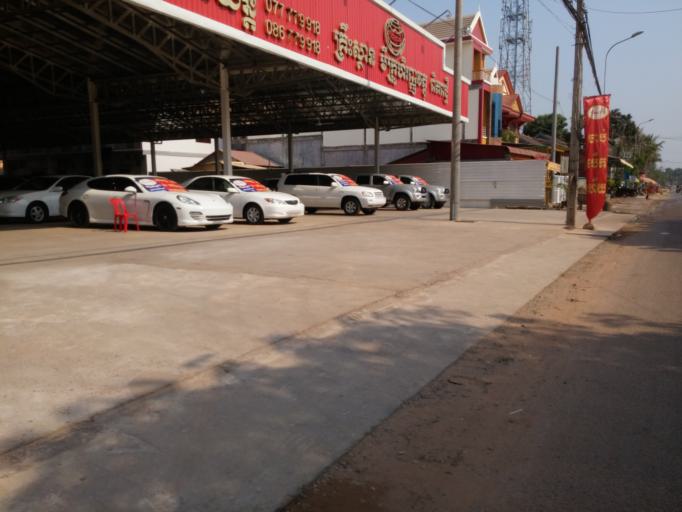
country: KH
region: Siem Reap
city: Siem Reap
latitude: 13.3691
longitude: 103.8489
